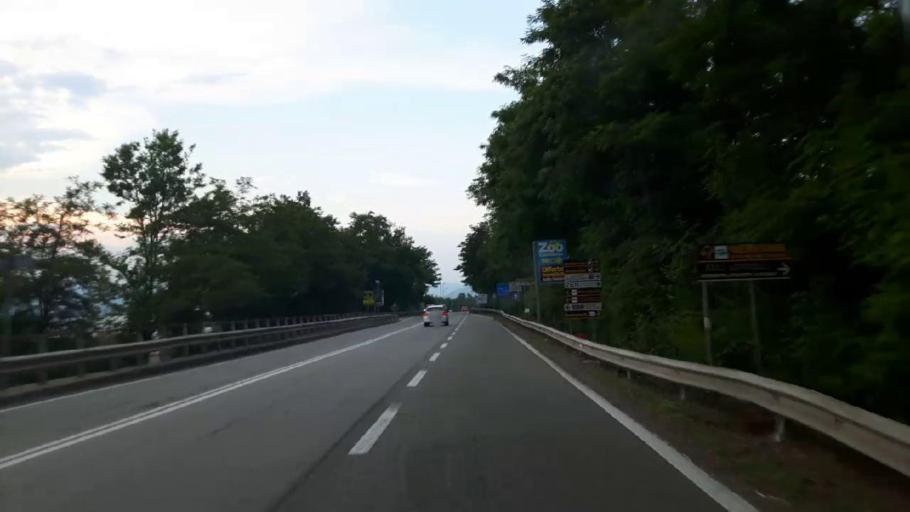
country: IT
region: Lombardy
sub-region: Provincia di Varese
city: Lisanza
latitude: 45.7167
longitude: 8.5916
